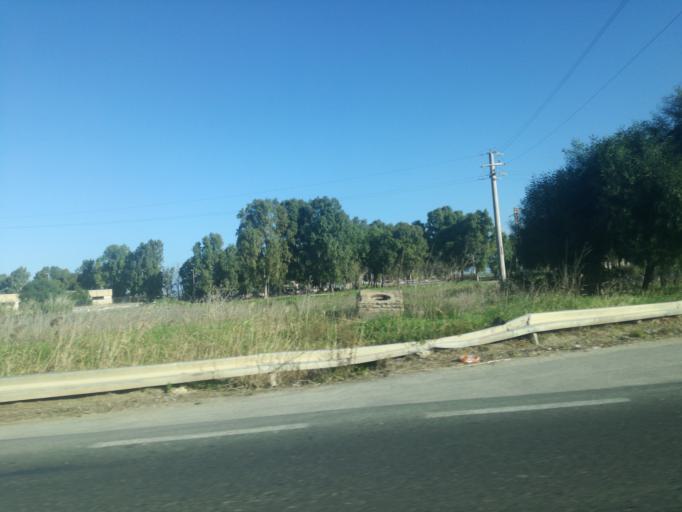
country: IT
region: Sicily
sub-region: Provincia di Caltanissetta
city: Gela
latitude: 37.0566
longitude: 14.2933
